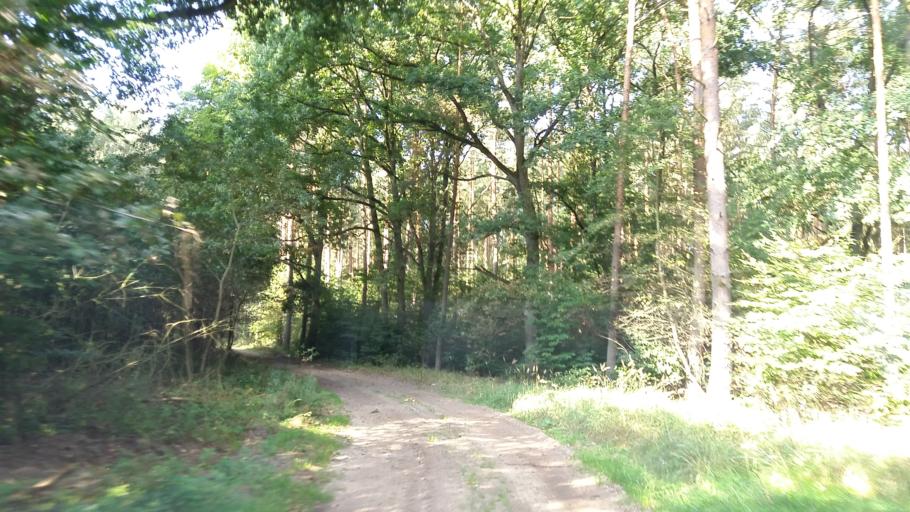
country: PL
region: West Pomeranian Voivodeship
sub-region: Powiat choszczenski
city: Choszczno
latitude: 53.2430
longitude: 15.4113
